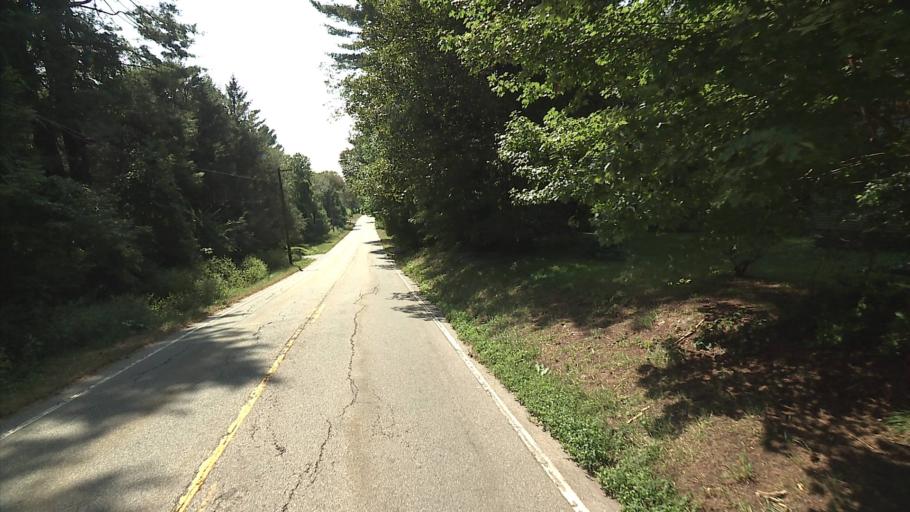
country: US
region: Connecticut
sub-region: Windham County
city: South Woodstock
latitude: 41.9186
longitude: -71.9564
